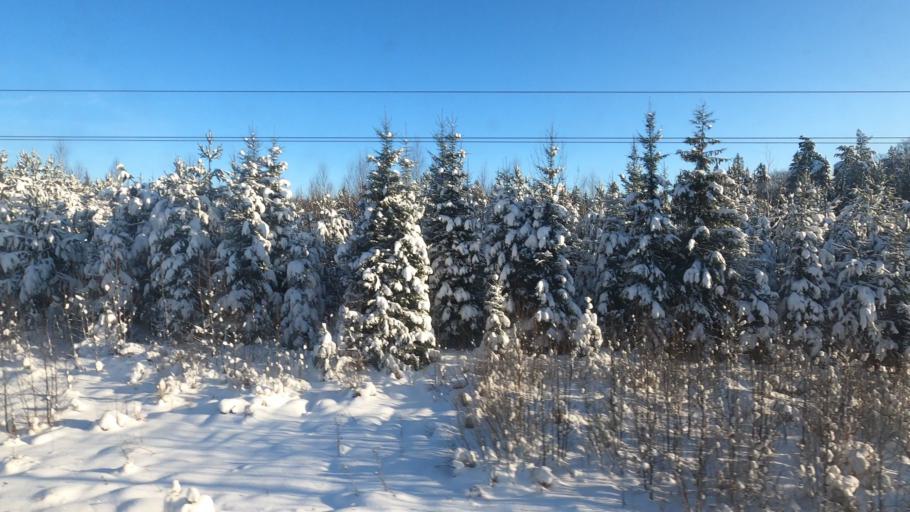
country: RU
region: Moskovskaya
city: Verbilki
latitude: 56.5228
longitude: 37.5578
